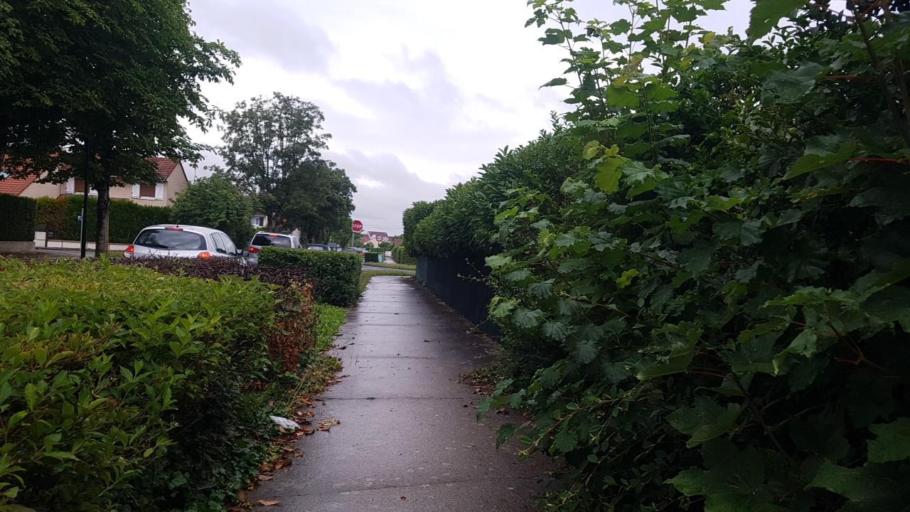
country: FR
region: Champagne-Ardenne
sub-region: Departement de la Marne
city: Vitry-le-Francois
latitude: 48.7331
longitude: 4.5974
